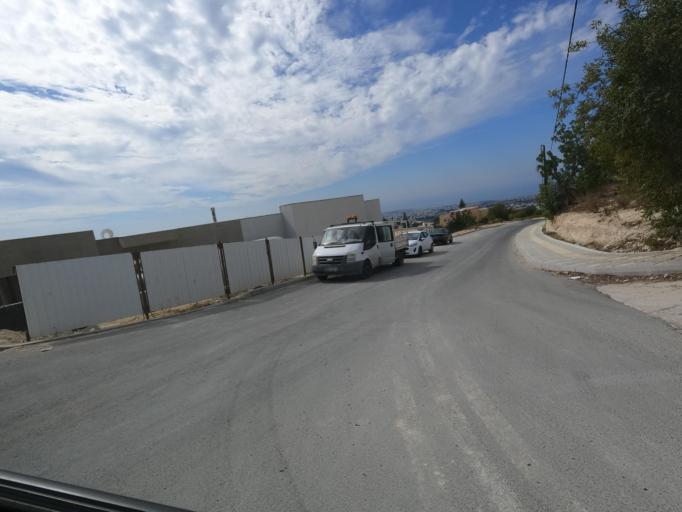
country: CY
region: Pafos
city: Mesogi
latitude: 34.8129
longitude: 32.4655
